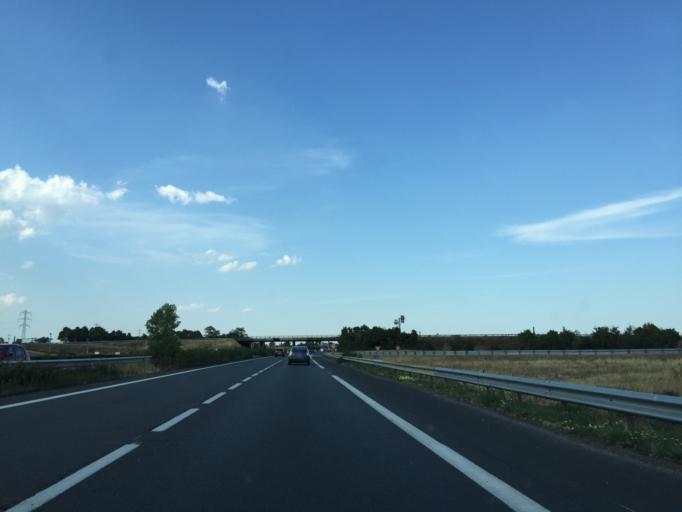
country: FR
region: Alsace
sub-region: Departement du Bas-Rhin
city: Chatenois
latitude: 48.2616
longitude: 7.4178
